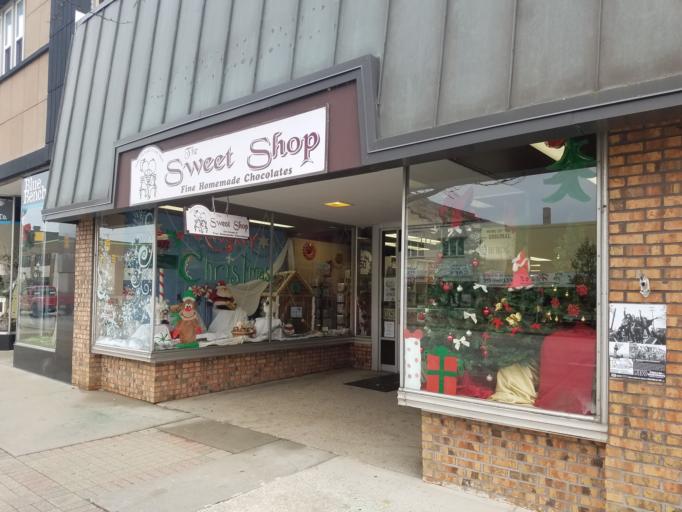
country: US
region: Michigan
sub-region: Wexford County
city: Cadillac
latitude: 44.2500
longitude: -85.3993
